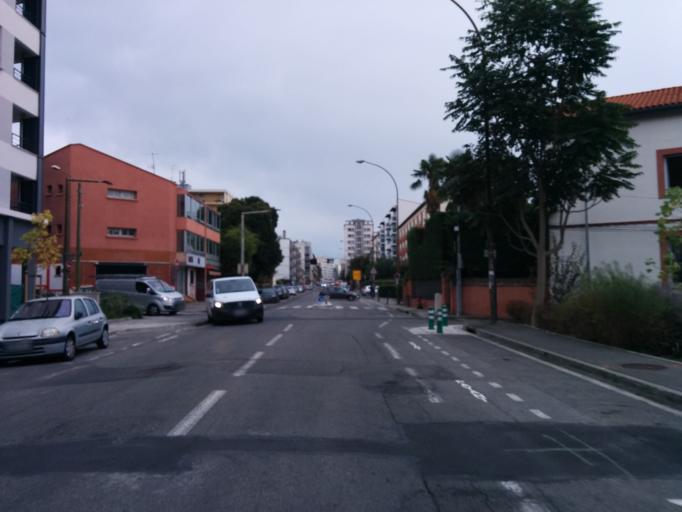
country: FR
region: Midi-Pyrenees
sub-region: Departement de la Haute-Garonne
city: Toulouse
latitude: 43.6029
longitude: 1.4204
